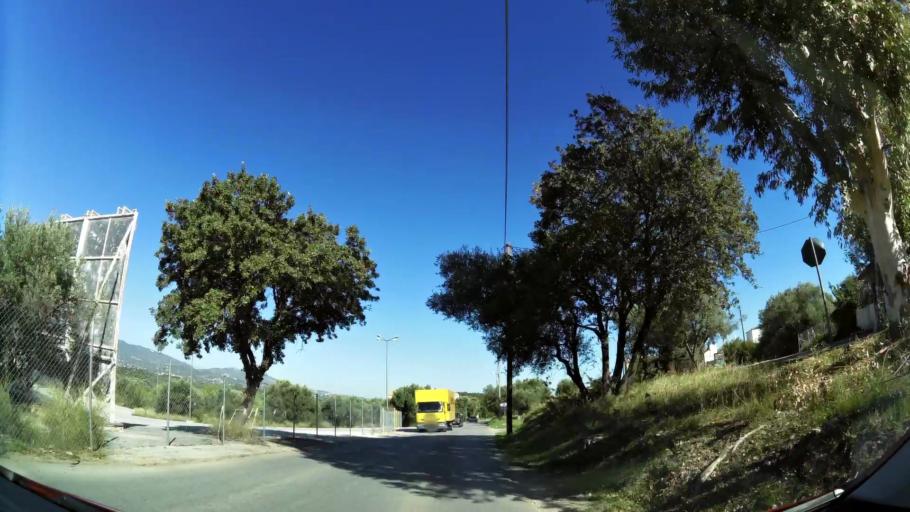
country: GR
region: Attica
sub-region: Nomarchia Anatolikis Attikis
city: Leondarion
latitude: 37.9727
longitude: 23.8592
